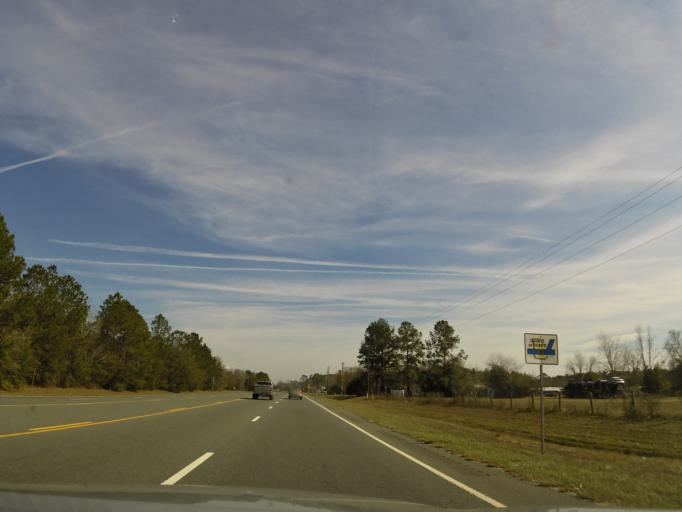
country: US
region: Georgia
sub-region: Pierce County
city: Blackshear
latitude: 31.1798
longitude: -82.1469
